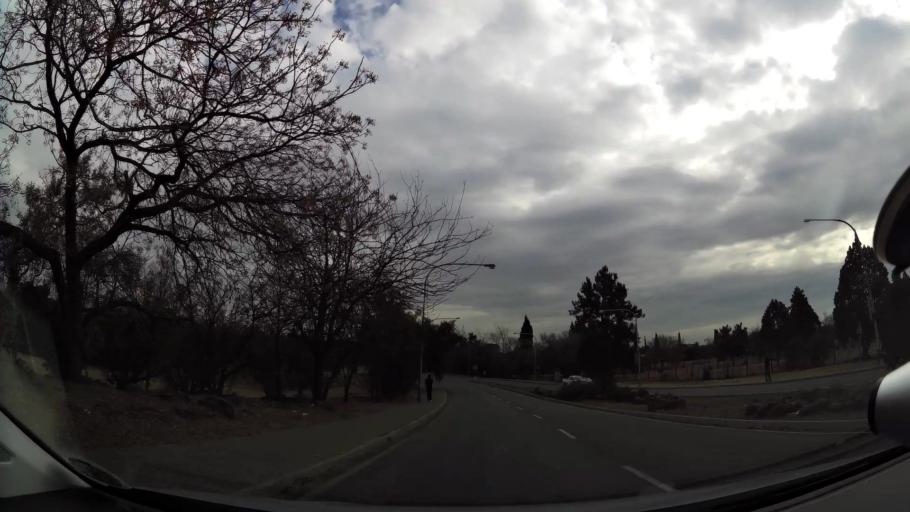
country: ZA
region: Orange Free State
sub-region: Fezile Dabi District Municipality
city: Kroonstad
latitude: -27.6728
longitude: 27.2383
